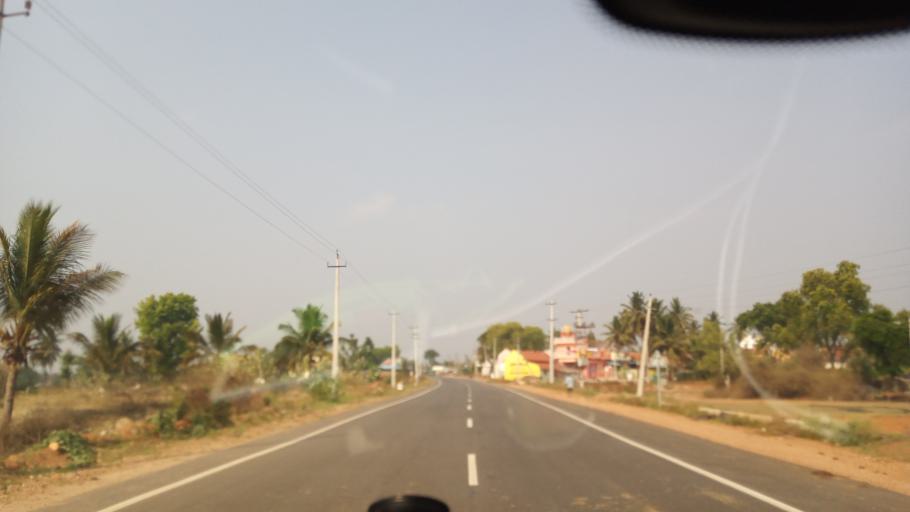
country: IN
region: Karnataka
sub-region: Mandya
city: Melukote
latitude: 12.7128
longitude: 76.7054
